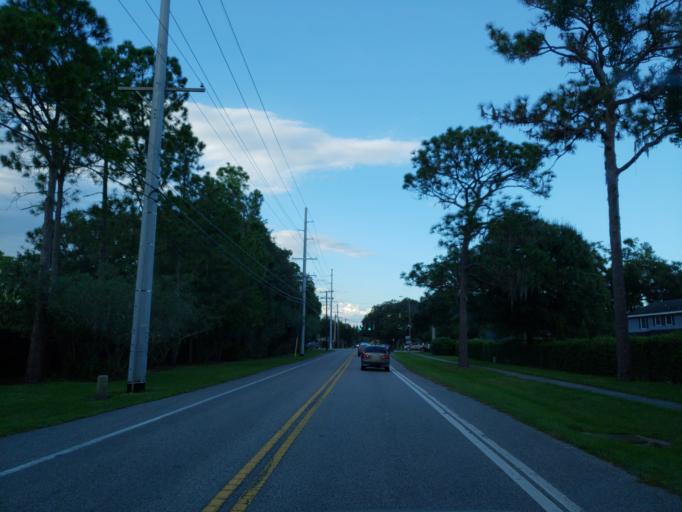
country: US
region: Florida
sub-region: Hillsborough County
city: Carrollwood Village
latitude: 28.0645
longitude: -82.5170
